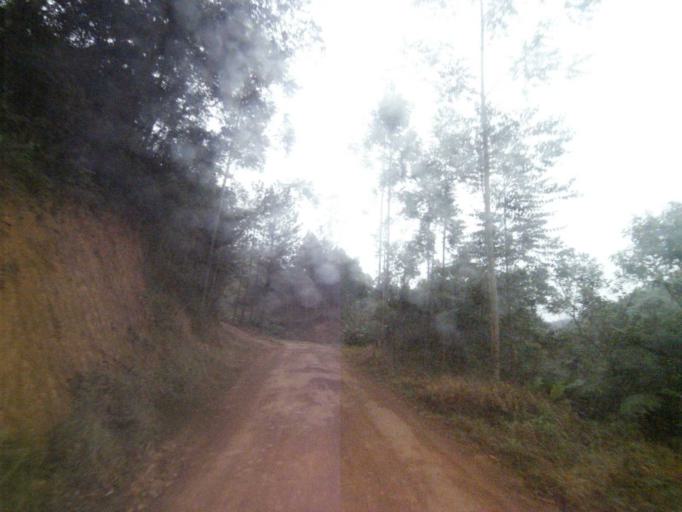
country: BR
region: Santa Catarina
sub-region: Anitapolis
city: Anitapolis
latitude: -27.8926
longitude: -49.1308
